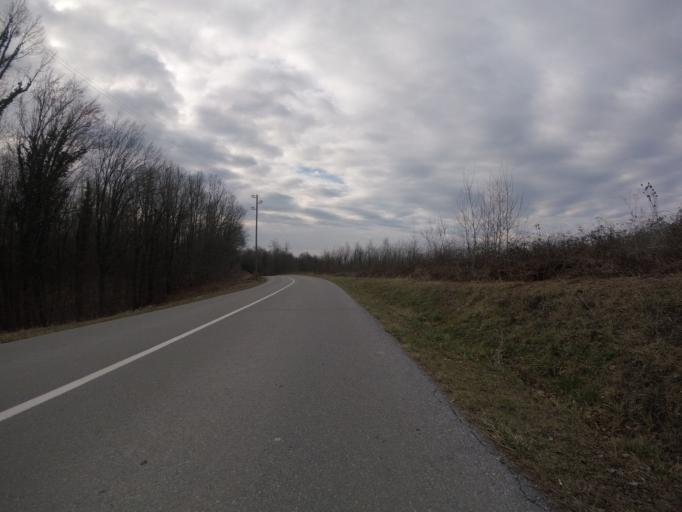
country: HR
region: Zagrebacka
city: Mraclin
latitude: 45.5502
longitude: 16.0554
